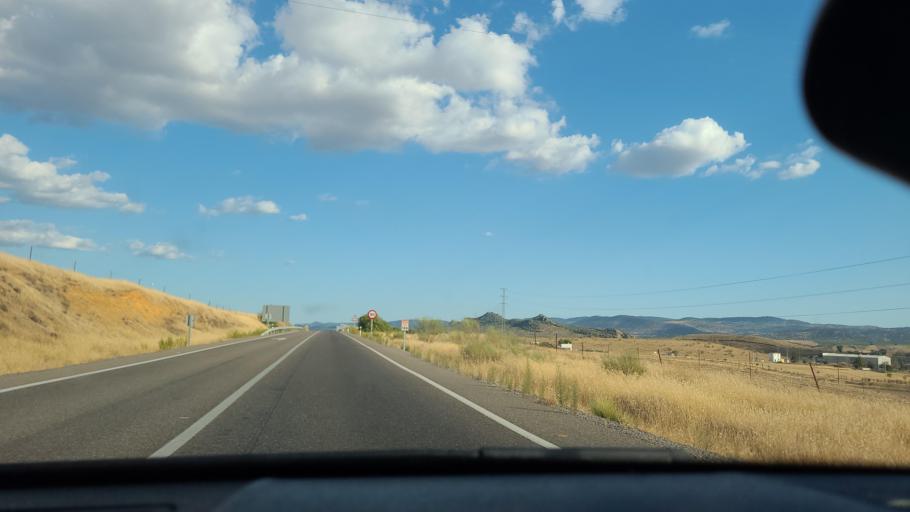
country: ES
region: Andalusia
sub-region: Province of Cordoba
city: Belmez
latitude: 38.2772
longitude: -5.2004
